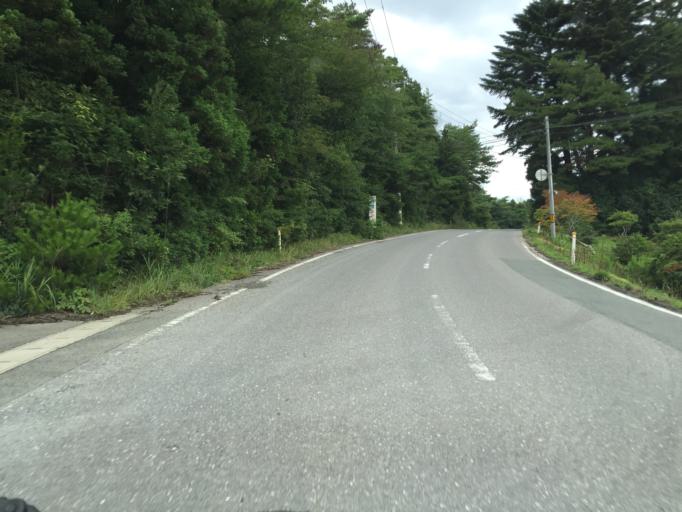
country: JP
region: Fukushima
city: Namie
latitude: 37.7459
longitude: 141.0013
